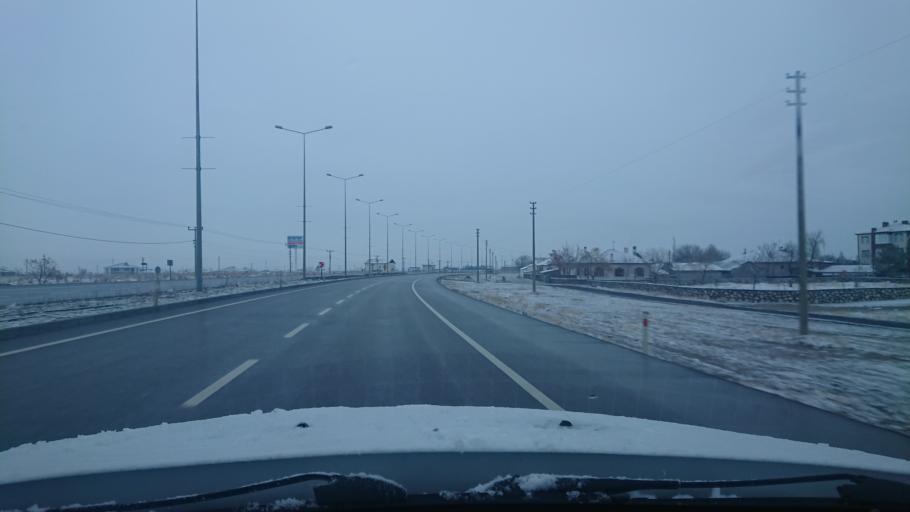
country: TR
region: Aksaray
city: Sultanhani
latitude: 38.2532
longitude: 33.5526
